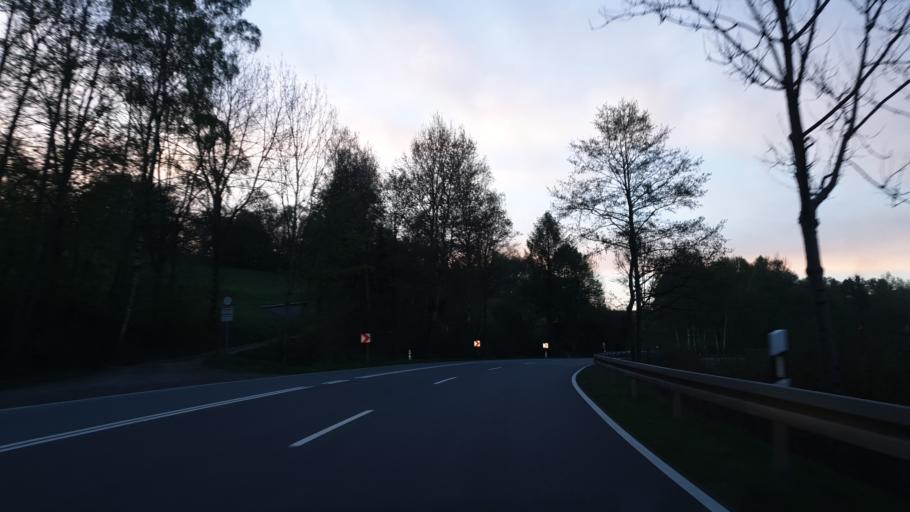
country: DE
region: Saxony
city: Lossnitz
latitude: 50.6336
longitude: 12.7333
